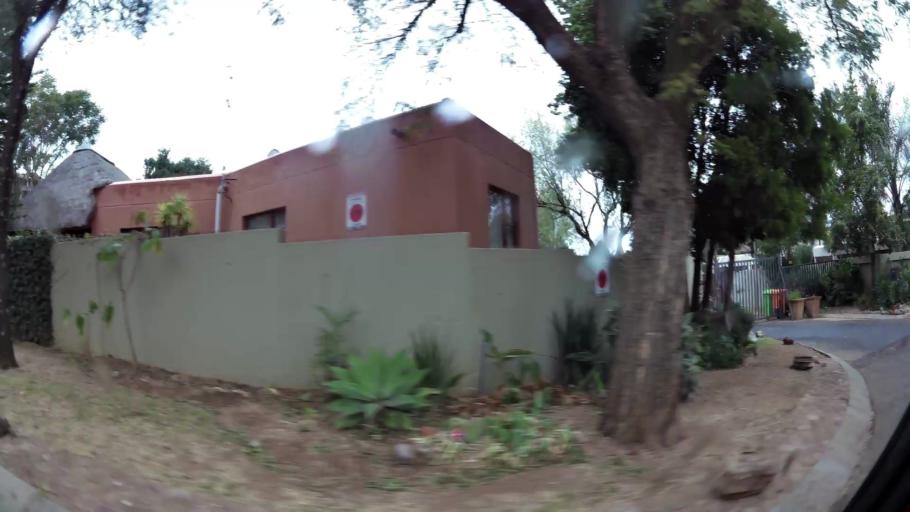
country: ZA
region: Gauteng
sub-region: City of Johannesburg Metropolitan Municipality
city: Roodepoort
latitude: -26.1163
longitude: 27.9143
